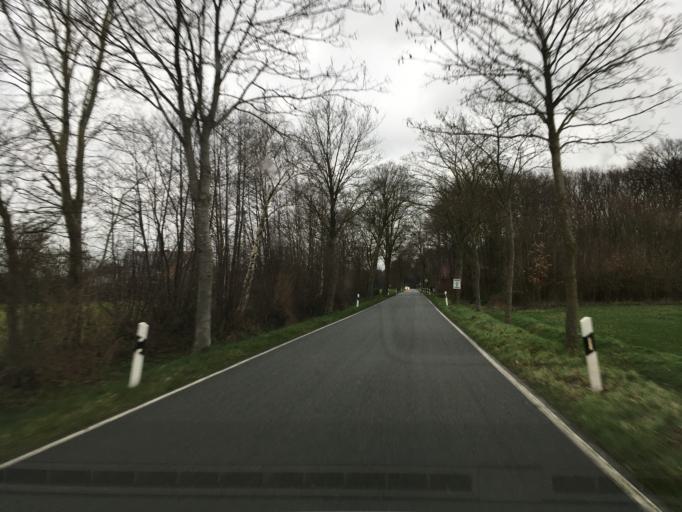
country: DE
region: North Rhine-Westphalia
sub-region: Regierungsbezirk Munster
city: Schoppingen
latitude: 52.0943
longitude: 7.1741
